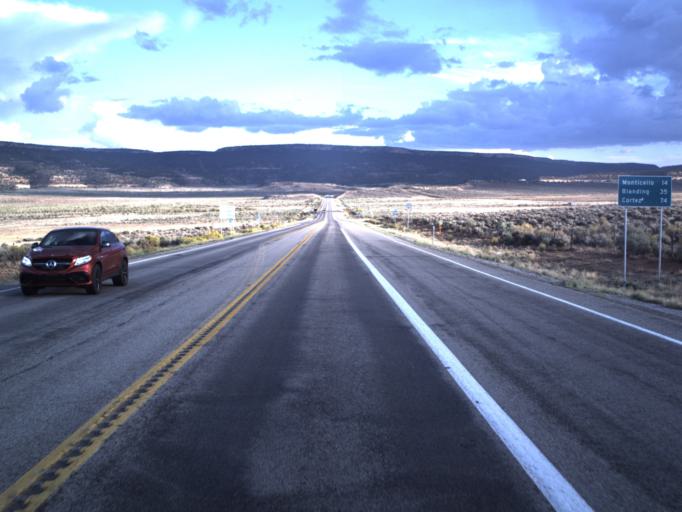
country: US
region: Utah
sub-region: San Juan County
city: Monticello
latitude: 38.0735
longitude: -109.3500
